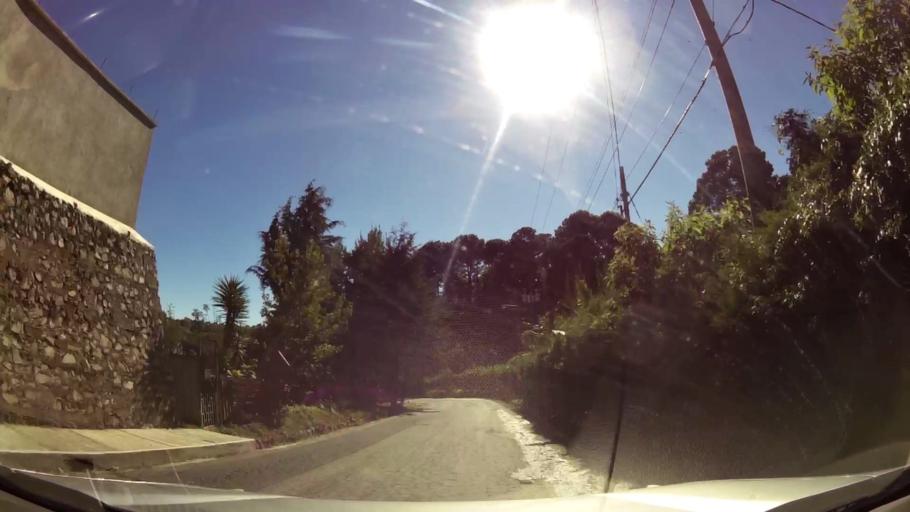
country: GT
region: Guatemala
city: Fraijanes
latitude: 14.4549
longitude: -90.4420
